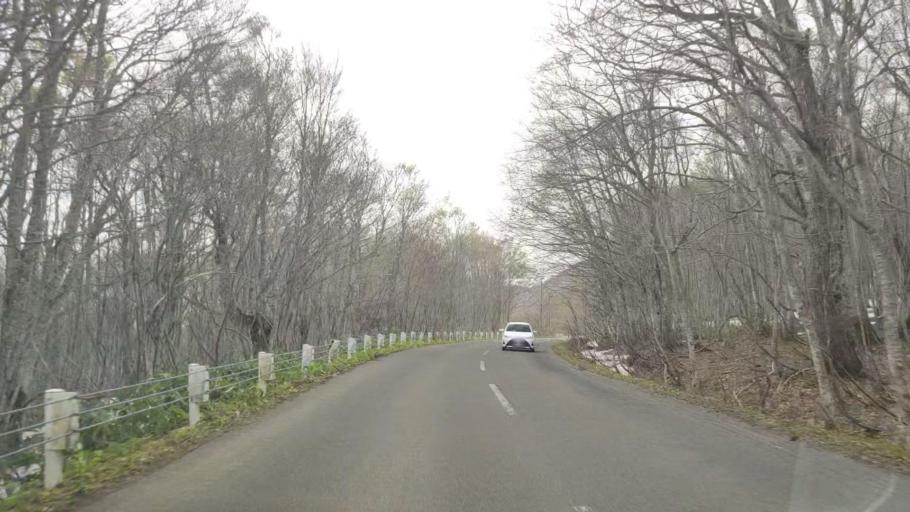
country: JP
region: Aomori
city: Aomori Shi
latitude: 40.6603
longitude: 140.9617
